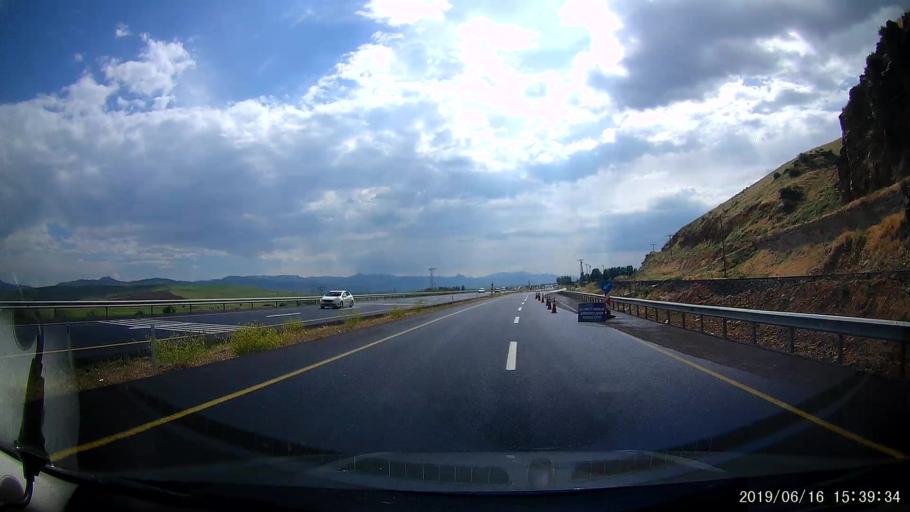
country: TR
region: Erzurum
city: Koprukoy
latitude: 39.9700
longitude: 41.8856
